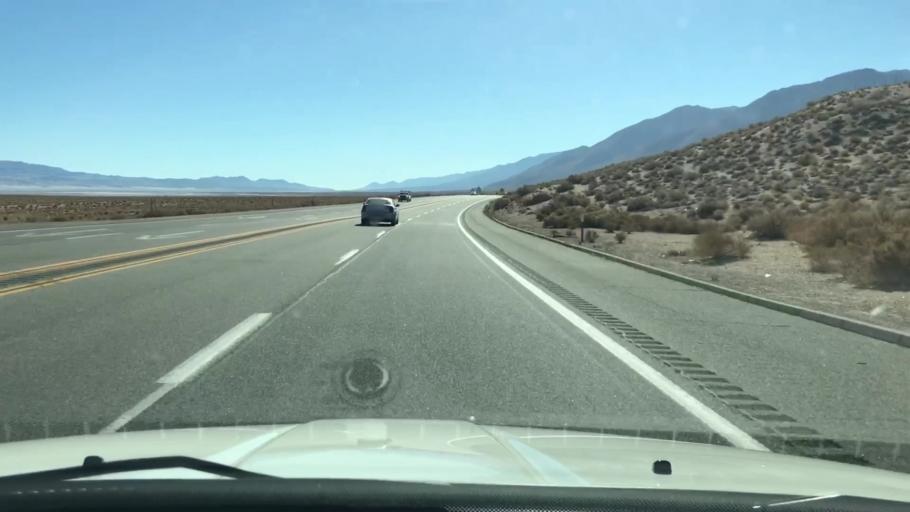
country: US
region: California
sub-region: Inyo County
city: Lone Pine
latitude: 36.5058
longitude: -118.0321
